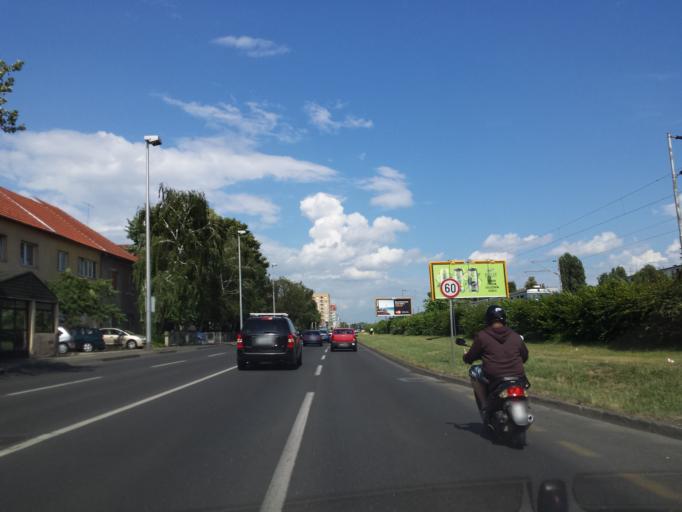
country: HR
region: Grad Zagreb
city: Zagreb
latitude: 45.8137
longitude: 16.0208
